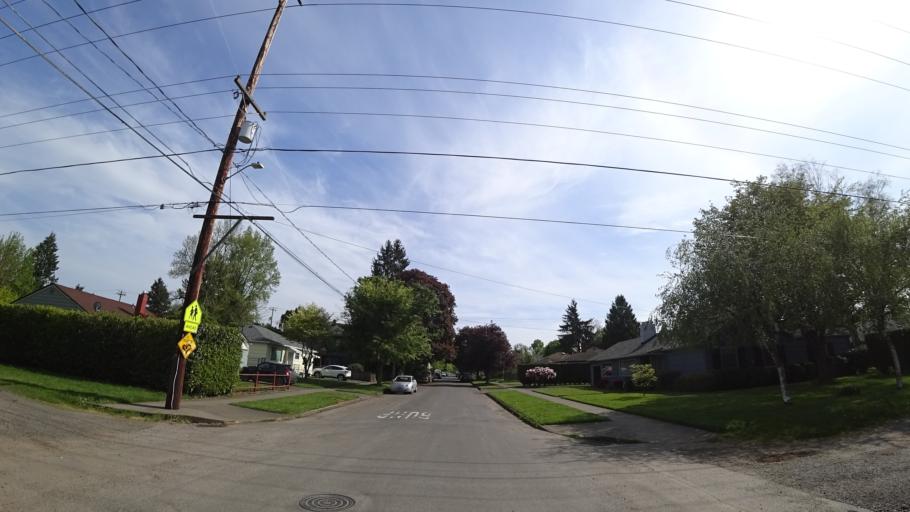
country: US
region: Oregon
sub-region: Clackamas County
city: Milwaukie
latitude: 45.4814
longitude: -122.6144
